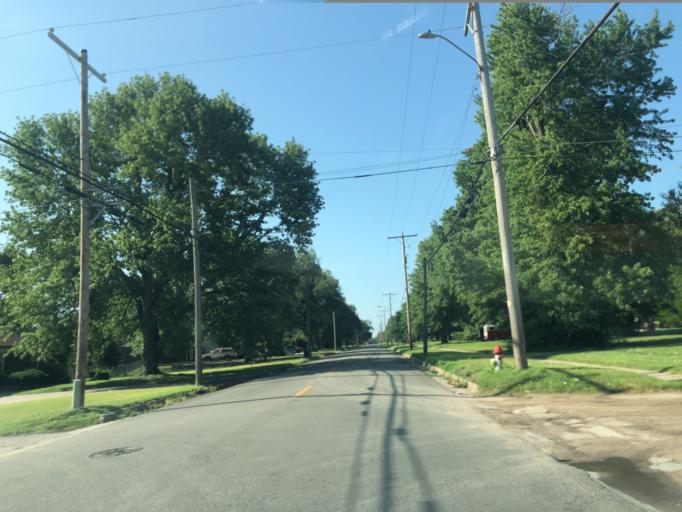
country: US
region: Kansas
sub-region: Sedgwick County
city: Wichita
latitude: 37.7434
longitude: -97.3449
